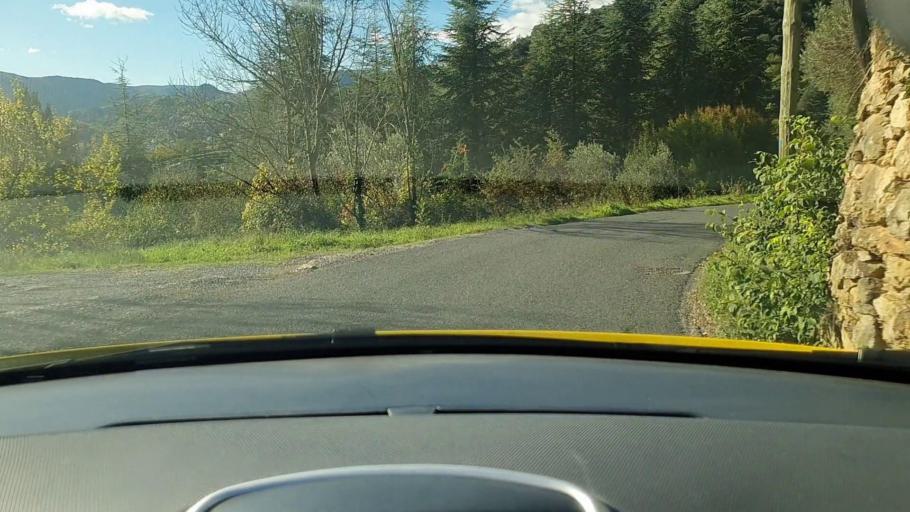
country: FR
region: Languedoc-Roussillon
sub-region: Departement du Gard
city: Le Vigan
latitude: 43.9952
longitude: 3.6233
